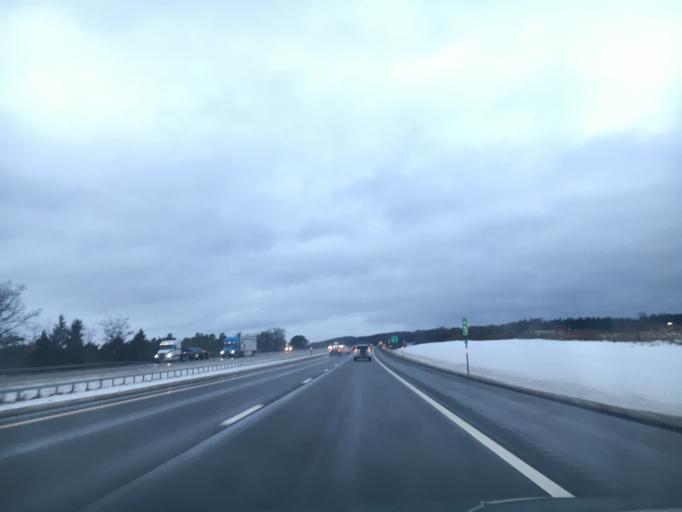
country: US
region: New York
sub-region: Cortland County
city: Homer
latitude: 42.7907
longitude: -76.1241
